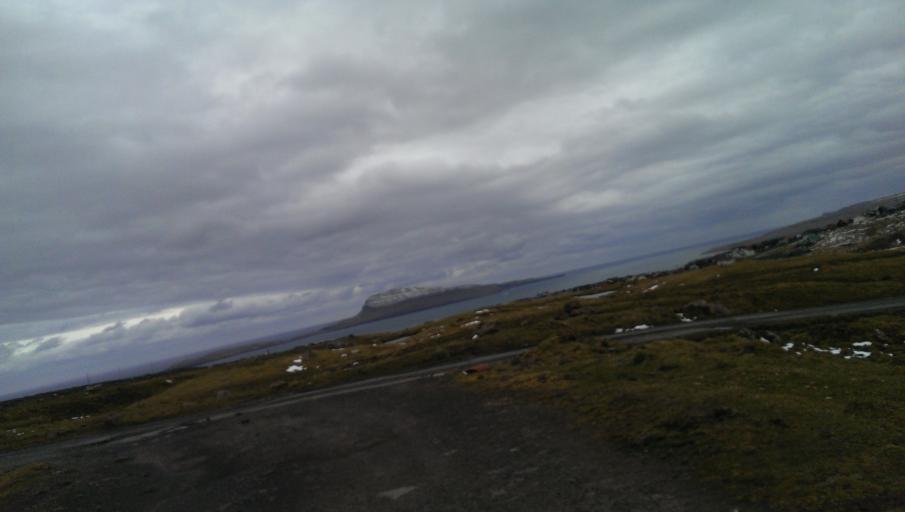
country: FO
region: Streymoy
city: Hoyvik
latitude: 62.0354
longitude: -6.8003
